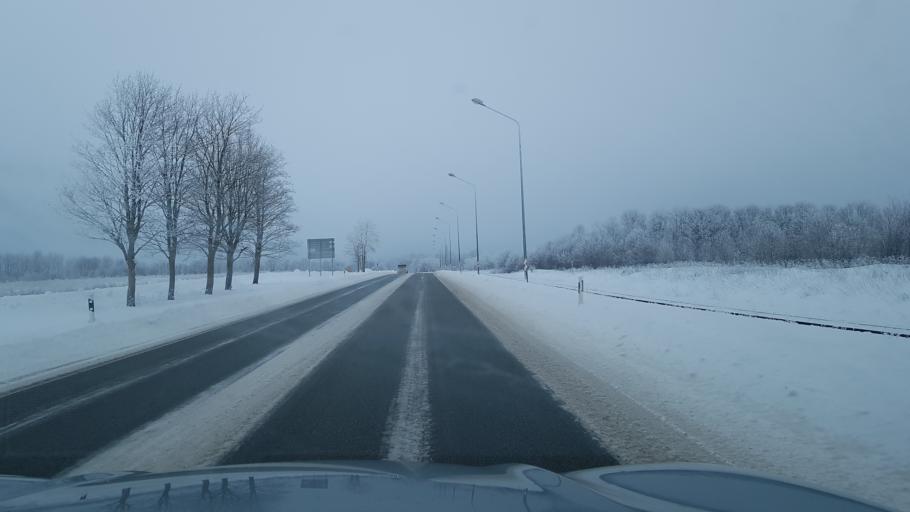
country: EE
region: Ida-Virumaa
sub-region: Johvi vald
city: Johvi
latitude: 59.3406
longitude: 27.4035
